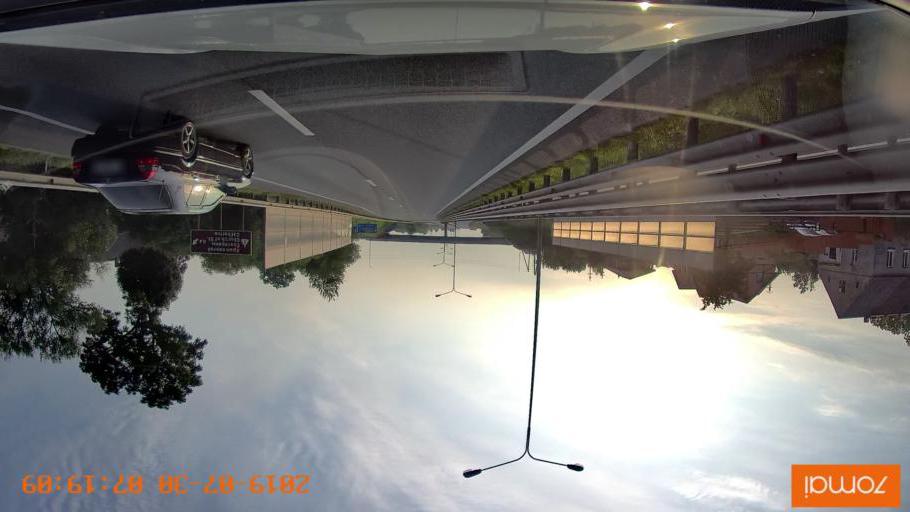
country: RU
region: Kaliningrad
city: Bol'shoe Isakovo
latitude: 54.7016
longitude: 20.6669
